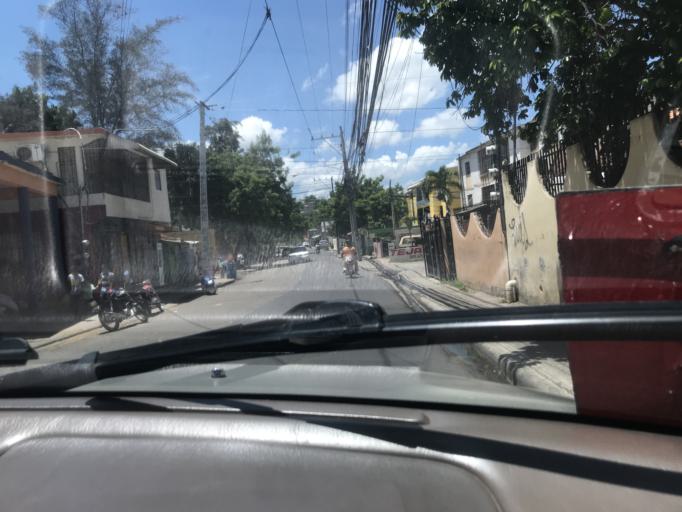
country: DO
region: Santiago
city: Santiago de los Caballeros
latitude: 19.4197
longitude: -70.6895
